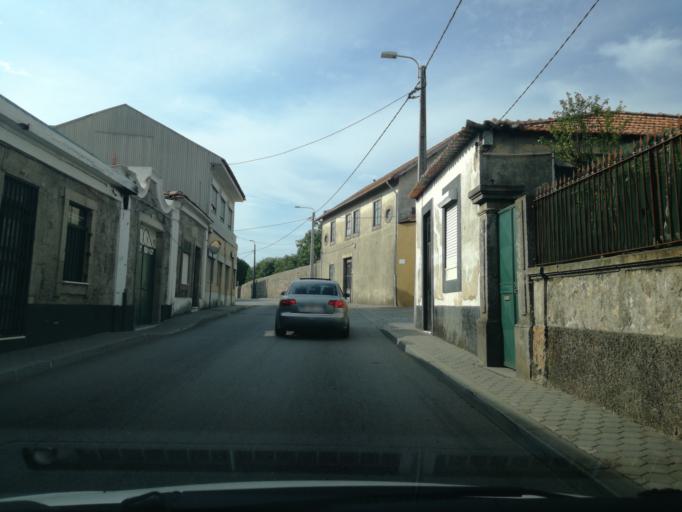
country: PT
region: Porto
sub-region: Vila Nova de Gaia
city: Azenha
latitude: 41.0791
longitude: -8.6248
